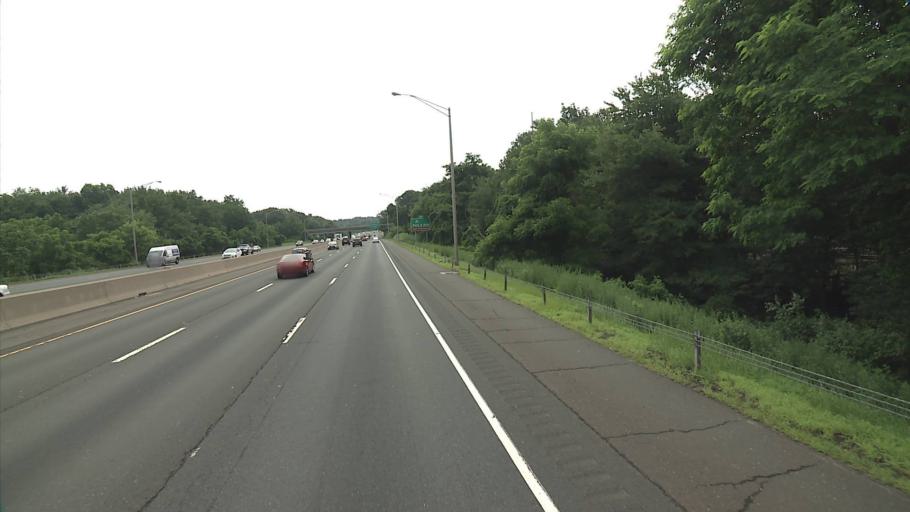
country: US
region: Connecticut
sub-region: Fairfield County
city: Westport
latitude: 41.1227
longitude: -73.3490
